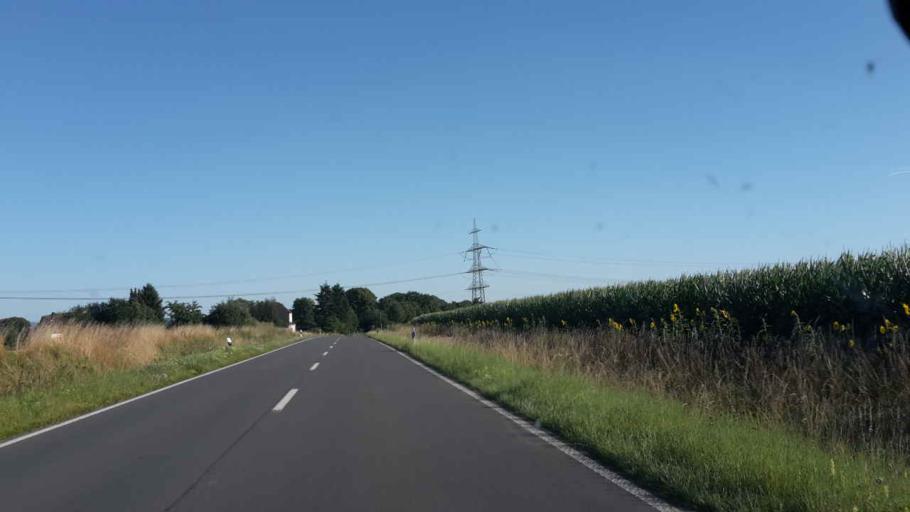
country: DE
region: North Rhine-Westphalia
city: Schwerte
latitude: 51.4657
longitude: 7.6049
